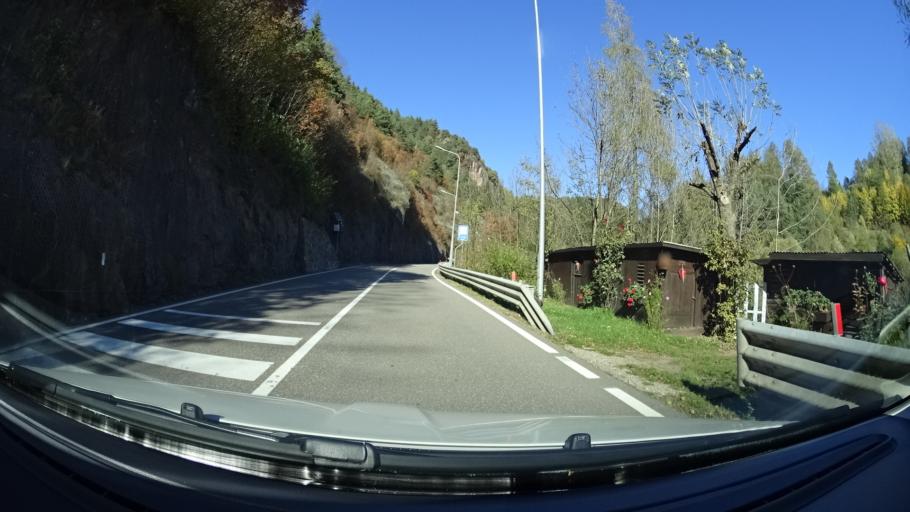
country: IT
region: Trentino-Alto Adige
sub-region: Provincia di Trento
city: Castello Molina di Fiemme
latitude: 46.2690
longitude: 11.4103
